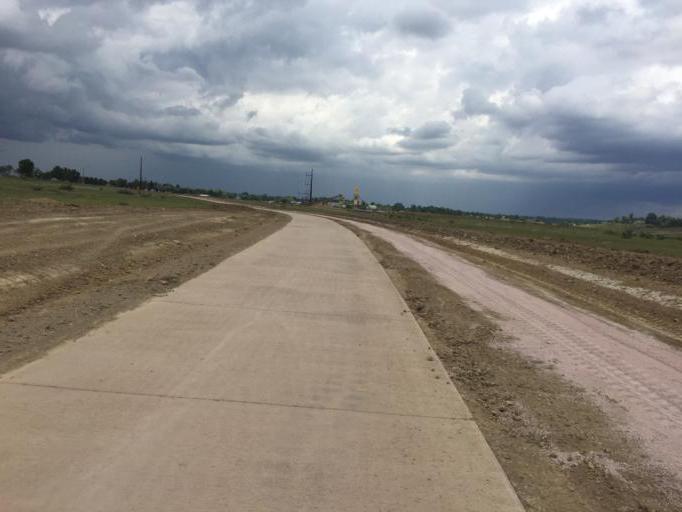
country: US
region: Colorado
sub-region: Larimer County
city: Loveland
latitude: 40.4892
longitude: -105.0954
